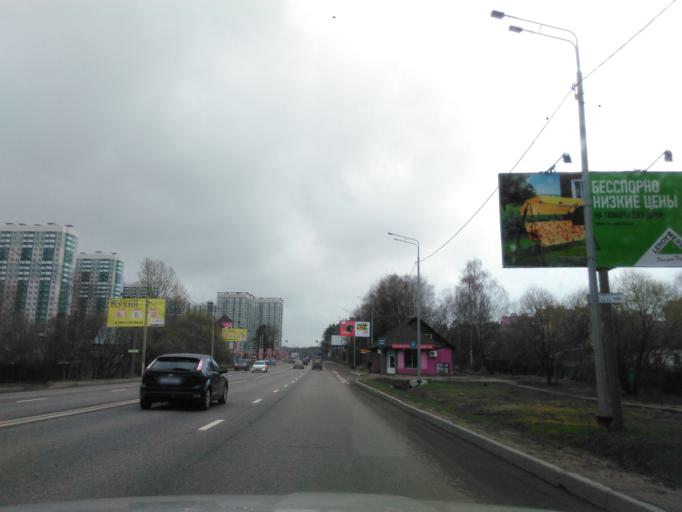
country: RU
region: Moskovskaya
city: Opalikha
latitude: 55.8375
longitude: 37.2590
